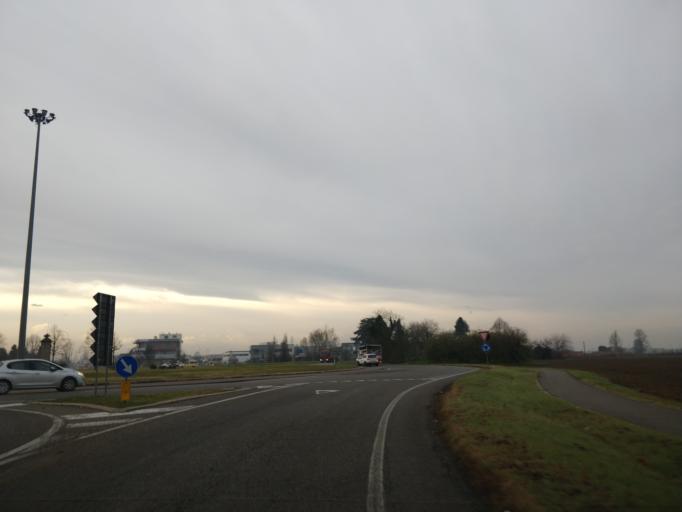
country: IT
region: Emilia-Romagna
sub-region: Provincia di Ferrara
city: Corpo Reno
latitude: 44.7500
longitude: 11.2994
